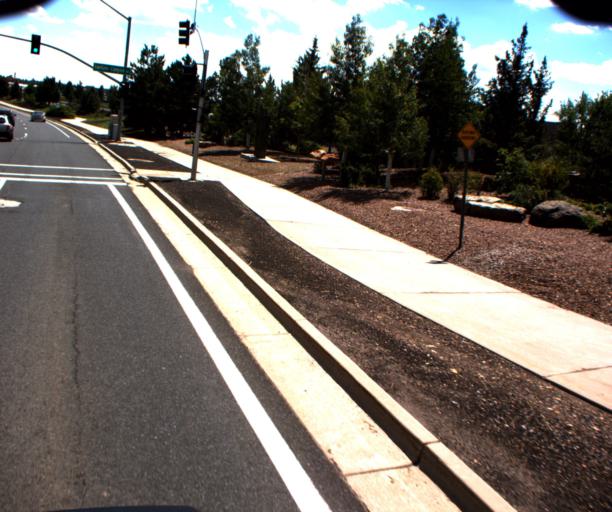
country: US
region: Arizona
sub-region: Coconino County
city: Flagstaff
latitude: 35.1936
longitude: -111.6347
